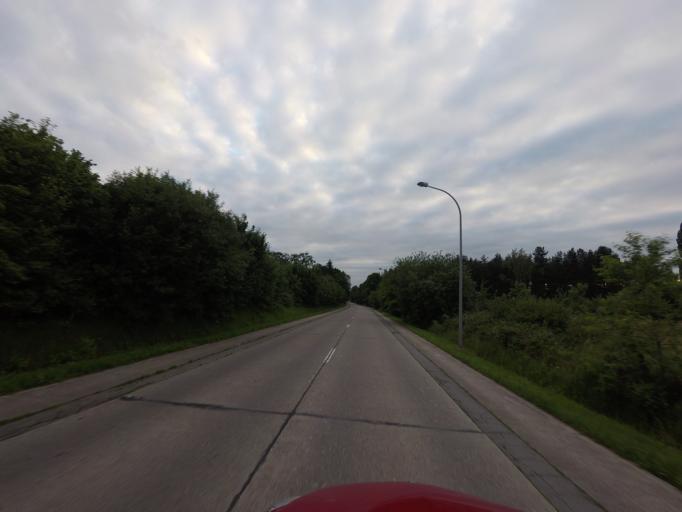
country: BE
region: Flanders
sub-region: Provincie Antwerpen
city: Berlaar
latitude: 51.1204
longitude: 4.6874
